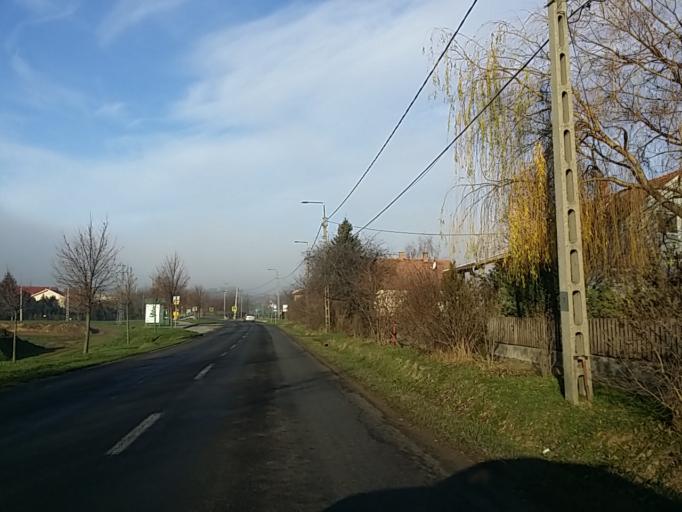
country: HU
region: Pest
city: Telki
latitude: 47.5500
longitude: 18.8223
